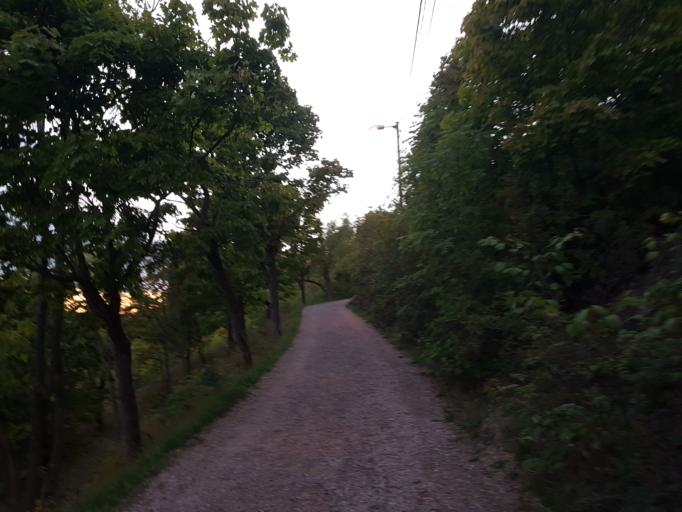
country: NO
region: Buskerud
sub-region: Drammen
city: Drammen
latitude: 59.7490
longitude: 10.2091
